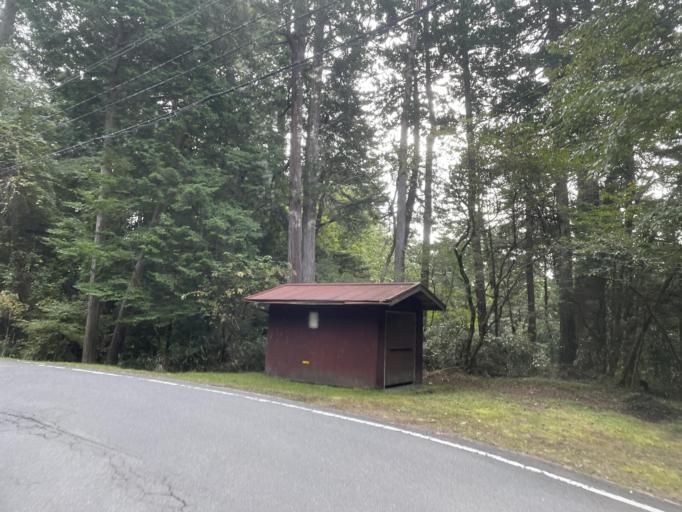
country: JP
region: Wakayama
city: Koya
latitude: 34.2237
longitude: 135.5754
